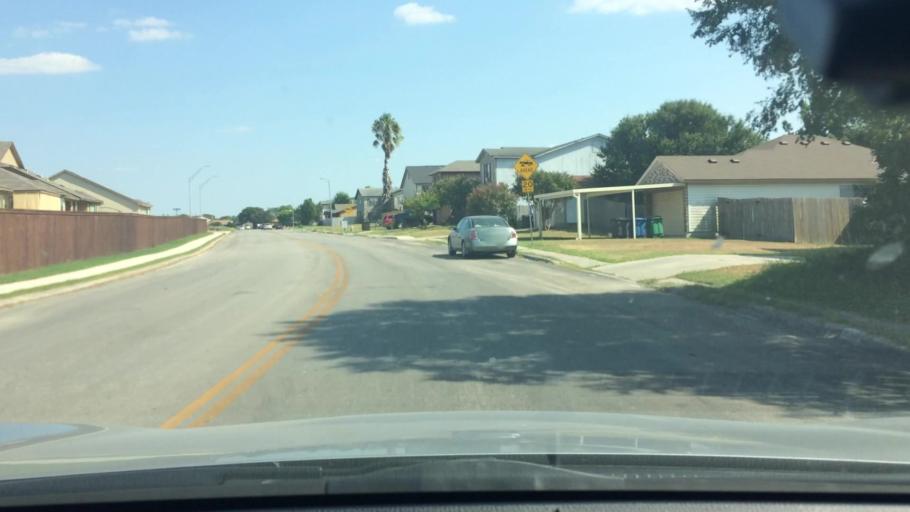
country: US
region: Texas
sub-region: Bexar County
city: Kirby
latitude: 29.4715
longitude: -98.3752
